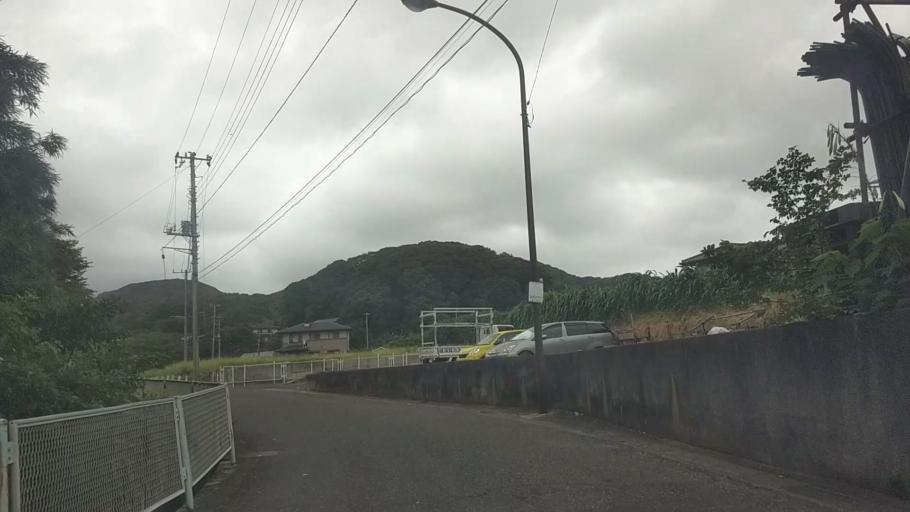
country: JP
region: Kanagawa
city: Hayama
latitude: 35.2310
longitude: 139.6242
